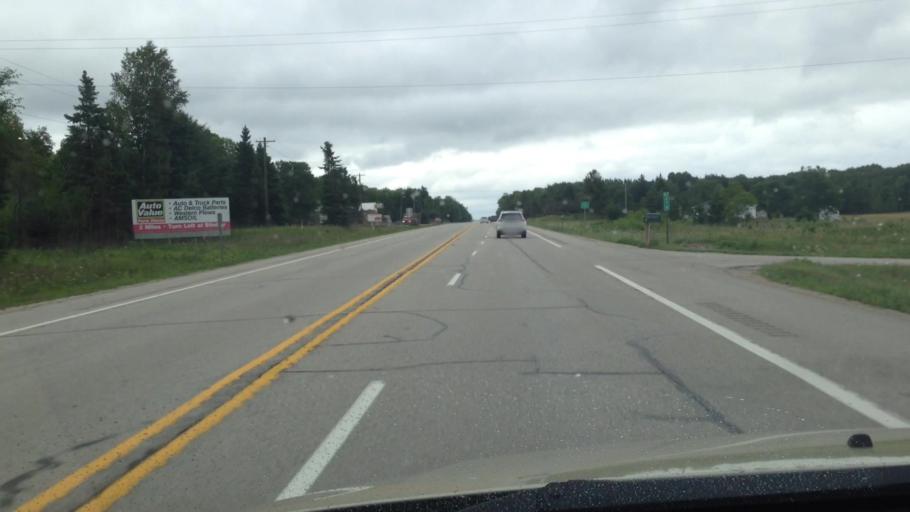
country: US
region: Michigan
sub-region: Luce County
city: Newberry
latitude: 46.1012
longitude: -85.6137
